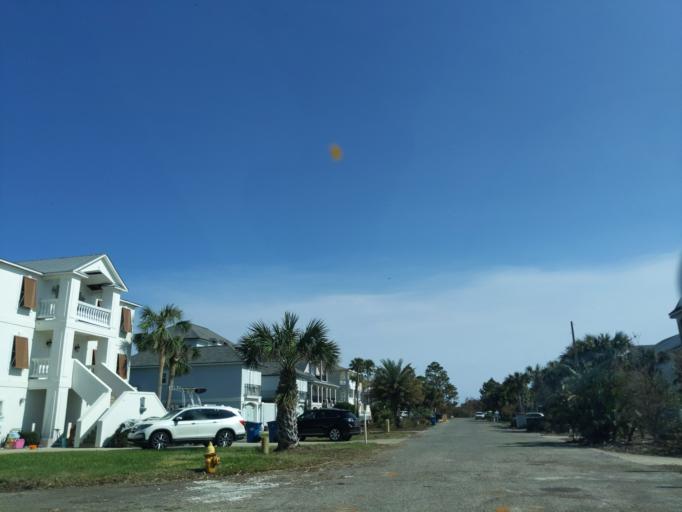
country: US
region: Florida
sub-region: Santa Rosa County
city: Gulf Breeze
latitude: 30.3494
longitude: -87.1876
